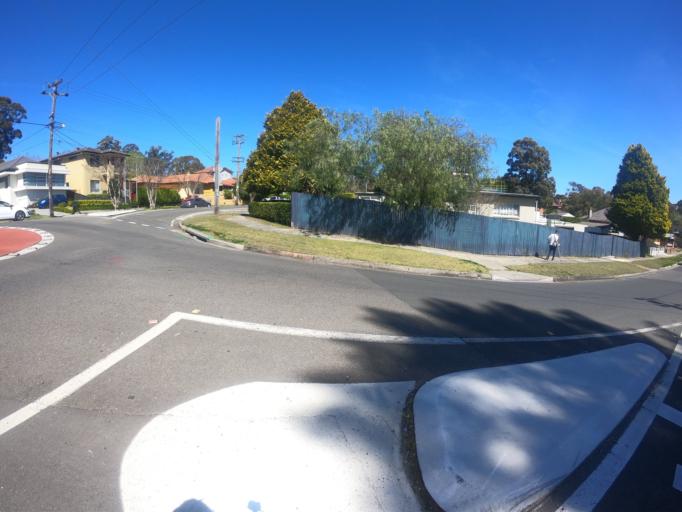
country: AU
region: New South Wales
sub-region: Ryde
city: East Ryde
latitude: -33.8190
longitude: 151.1282
